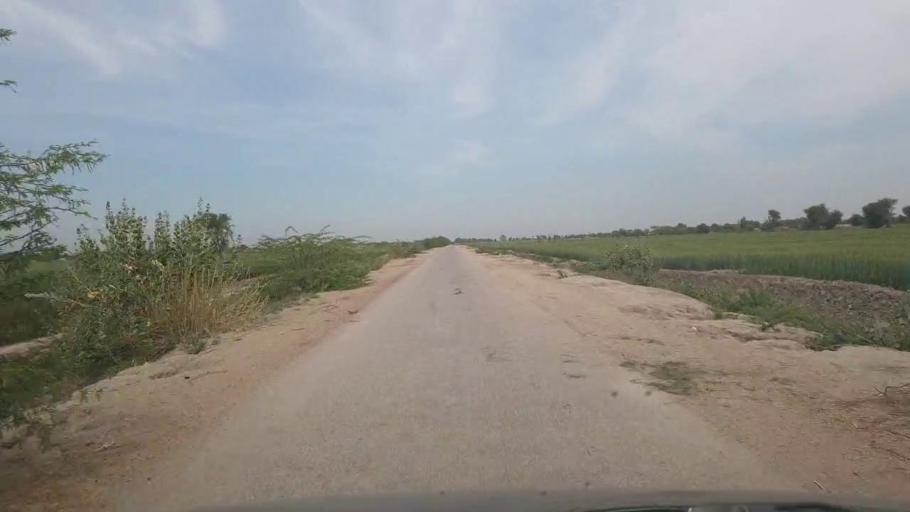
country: PK
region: Sindh
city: Kunri
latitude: 25.2496
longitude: 69.6230
